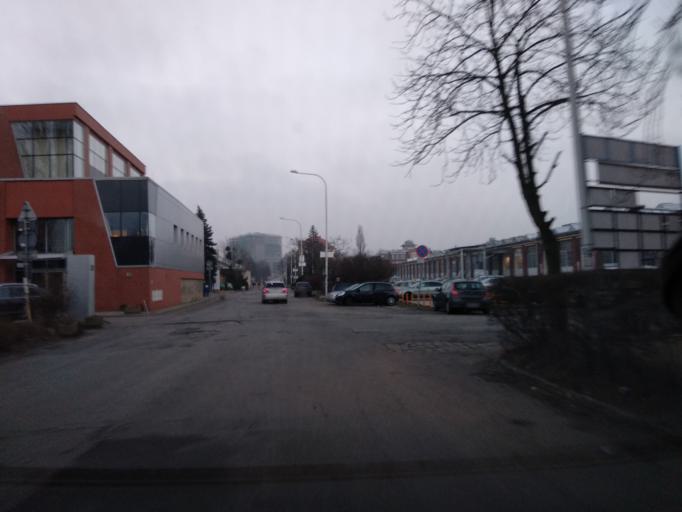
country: PL
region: Lower Silesian Voivodeship
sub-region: Powiat wroclawski
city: Wroclaw
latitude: 51.1123
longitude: 16.9854
